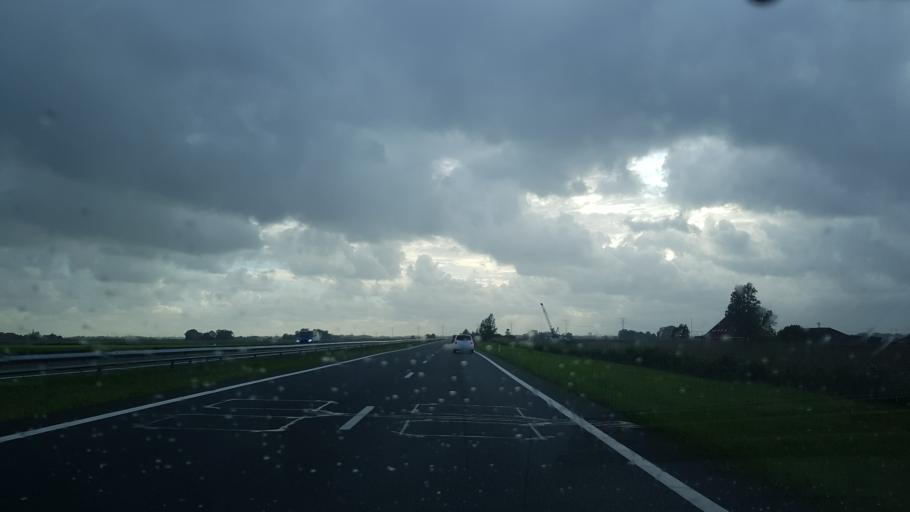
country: NL
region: Friesland
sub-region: Gemeente Boarnsterhim
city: Warten
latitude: 53.1694
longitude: 5.8909
